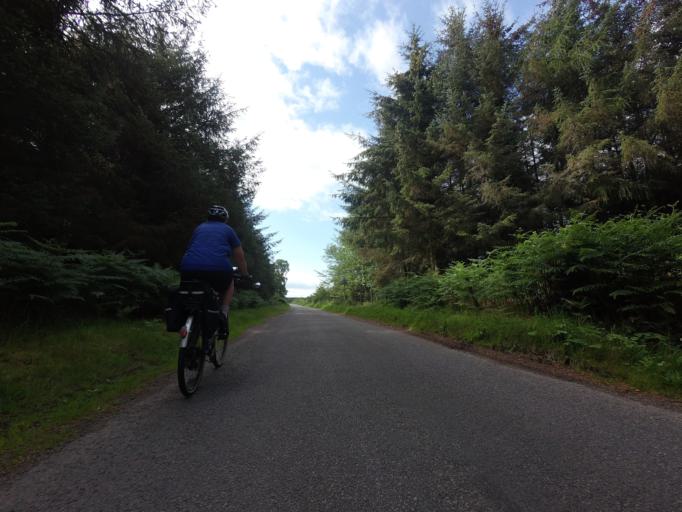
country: GB
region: Scotland
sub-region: Highland
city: Nairn
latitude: 57.5670
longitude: -3.8664
